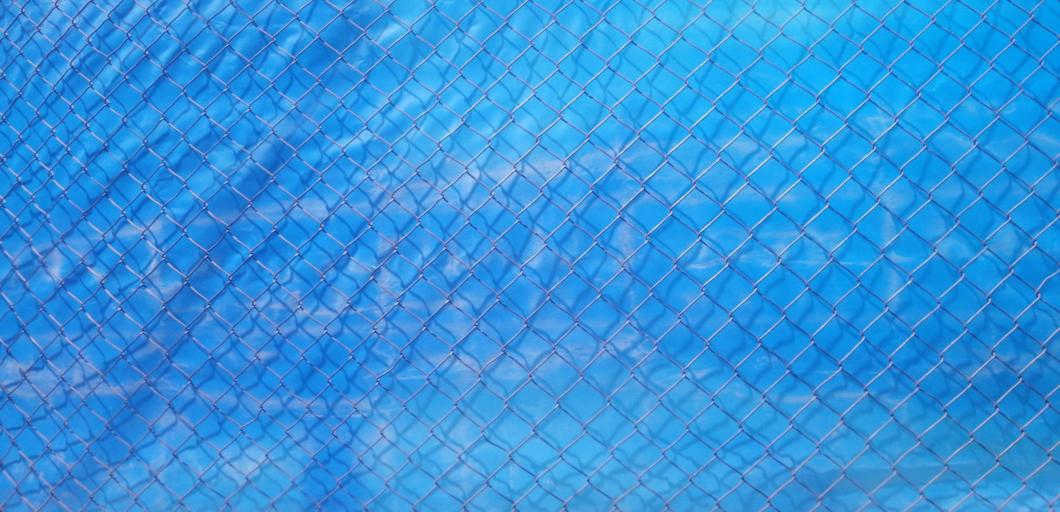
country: GT
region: Quetzaltenango
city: Quetzaltenango
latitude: 14.8307
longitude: -91.5327
